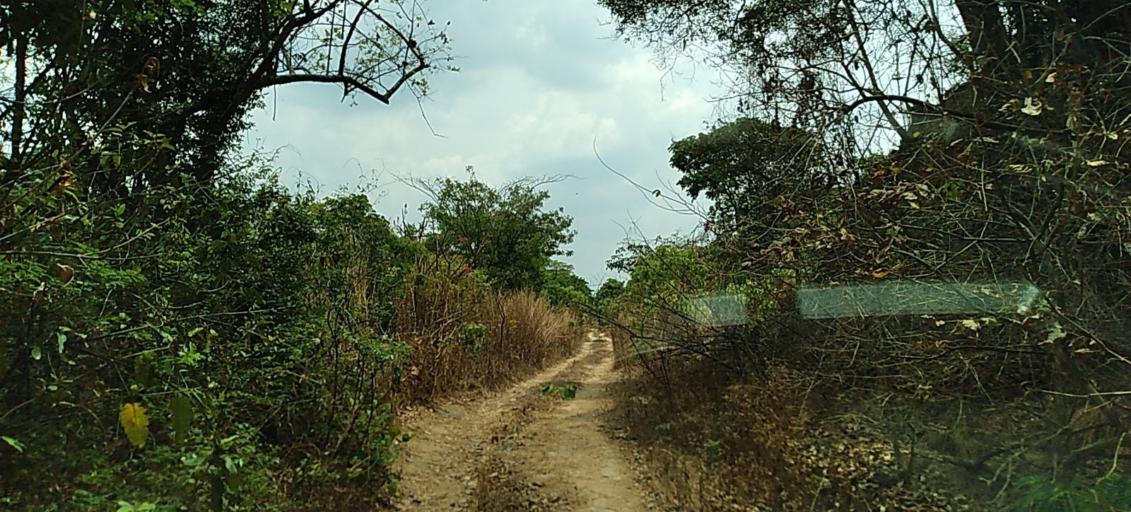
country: ZM
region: Copperbelt
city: Chililabombwe
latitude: -12.3293
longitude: 27.7699
